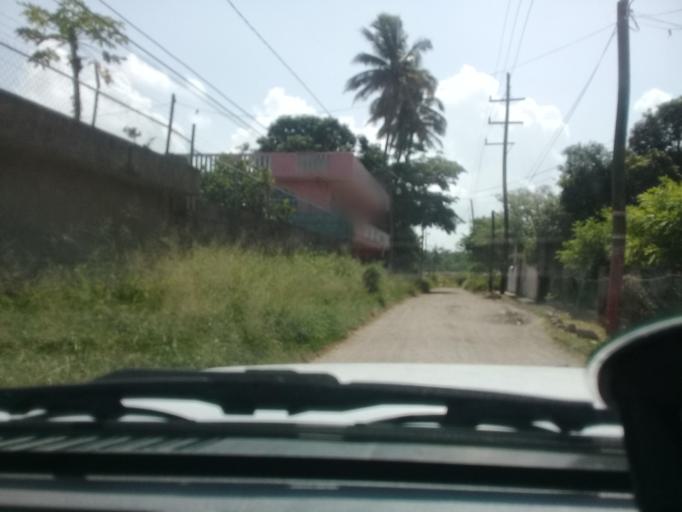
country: MX
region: Veracruz
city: Moralillo
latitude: 22.2262
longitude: -97.9006
